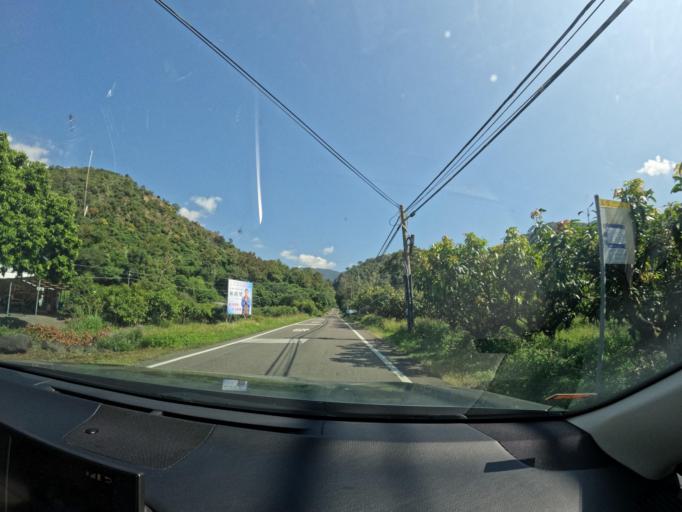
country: TW
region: Taiwan
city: Yujing
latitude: 23.1114
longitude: 120.7123
